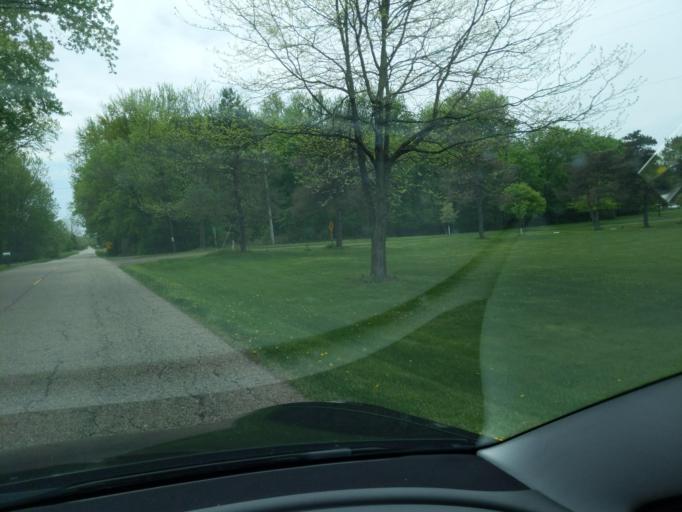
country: US
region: Michigan
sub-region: Ingham County
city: Holt
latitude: 42.5705
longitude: -84.5425
